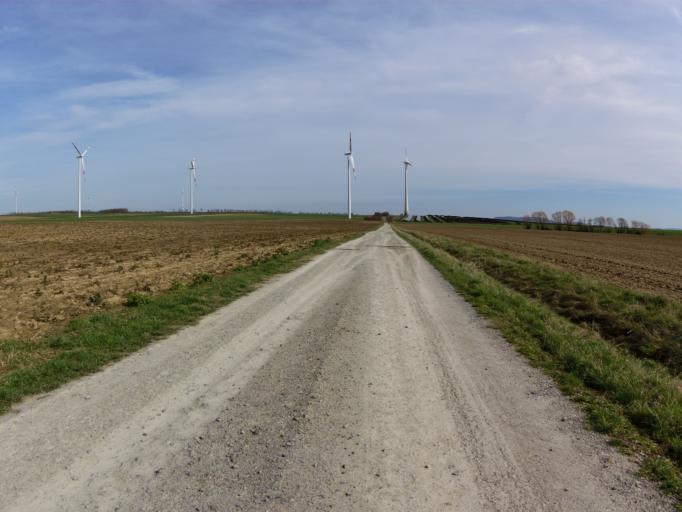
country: DE
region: Bavaria
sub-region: Regierungsbezirk Unterfranken
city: Biebelried
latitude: 49.7524
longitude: 10.0883
